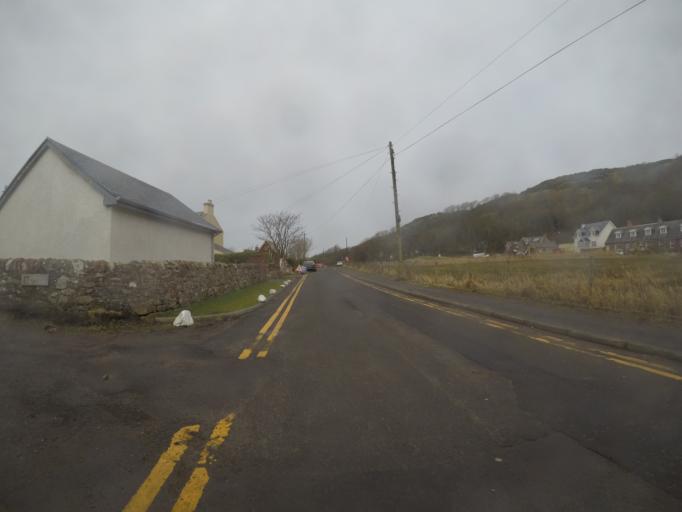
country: GB
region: Scotland
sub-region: North Ayrshire
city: West Kilbride
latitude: 55.6993
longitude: -4.9036
